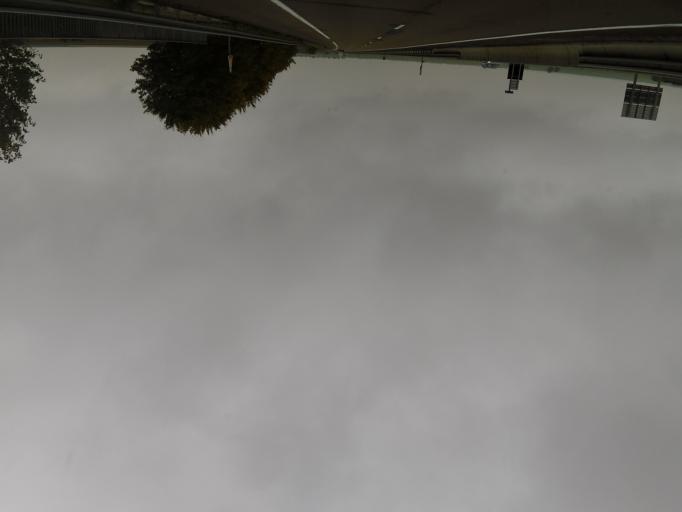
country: FR
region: Champagne-Ardenne
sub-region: Departement de la Marne
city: Verzy
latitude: 49.1116
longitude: 4.2519
